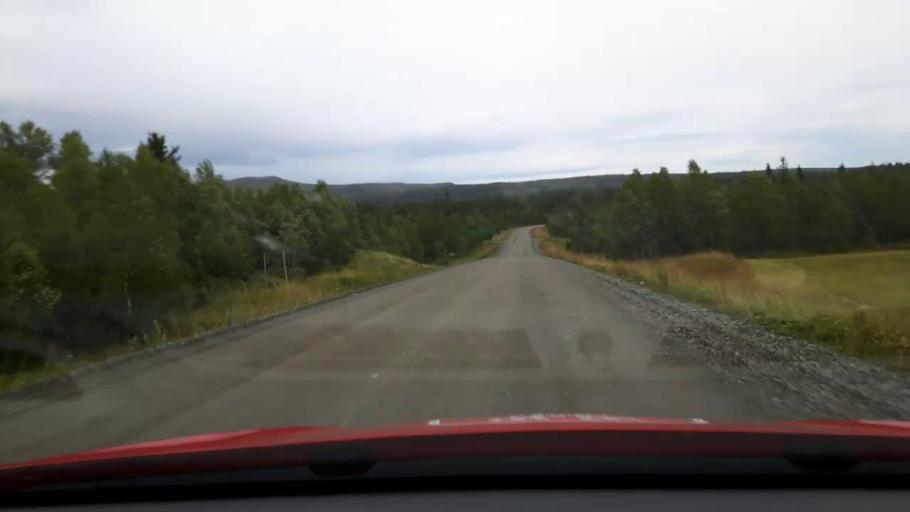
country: NO
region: Nord-Trondelag
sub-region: Meraker
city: Meraker
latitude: 63.5610
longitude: 12.3513
